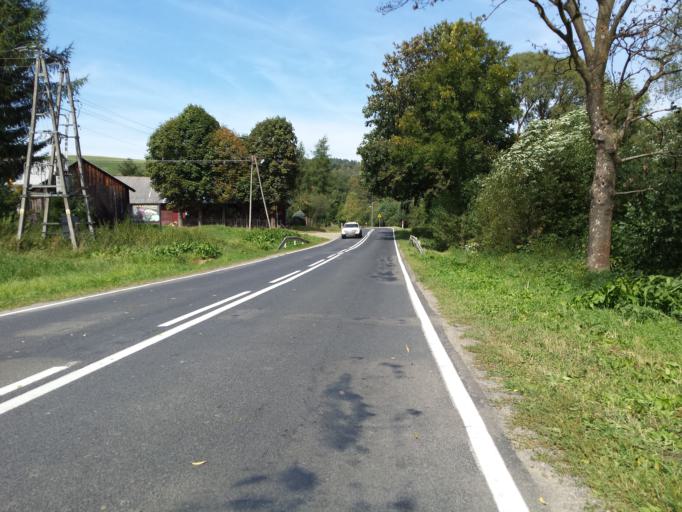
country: PL
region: Subcarpathian Voivodeship
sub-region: Powiat leski
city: Baligrod
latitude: 49.3598
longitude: 22.2794
